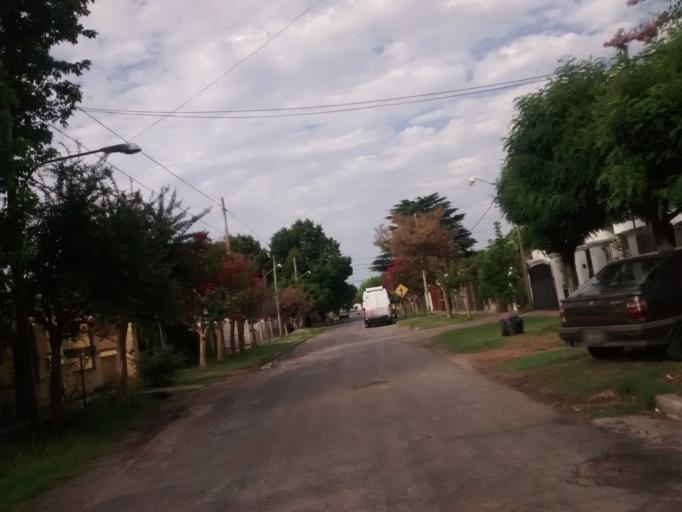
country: AR
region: Buenos Aires
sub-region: Partido de La Plata
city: La Plata
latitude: -34.8580
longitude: -58.0766
